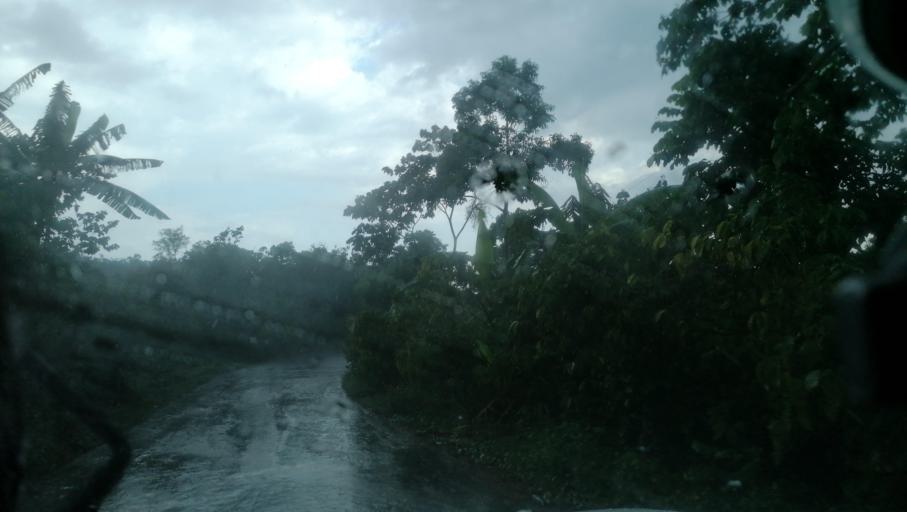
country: MX
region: Chiapas
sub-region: Cacahoatan
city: Benito Juarez
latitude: 15.0667
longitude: -92.1908
